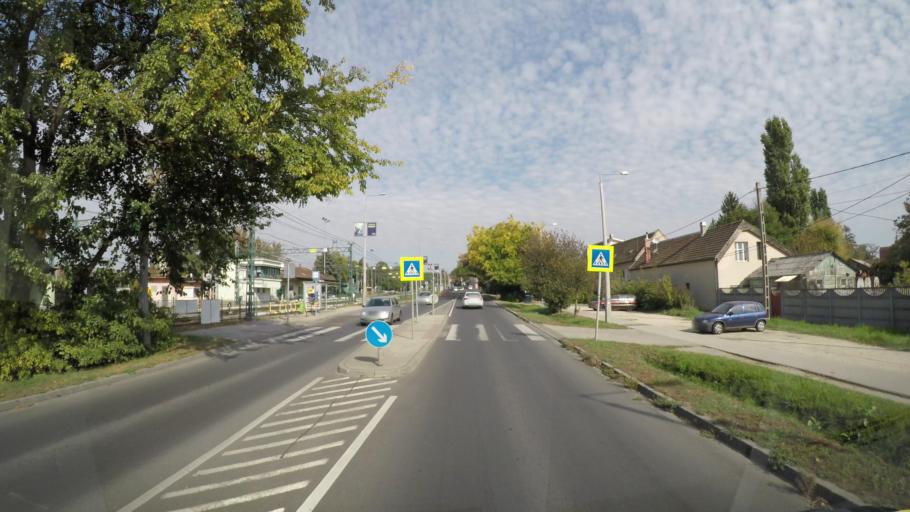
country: HU
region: Pest
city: Csomor
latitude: 47.5191
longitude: 19.2170
